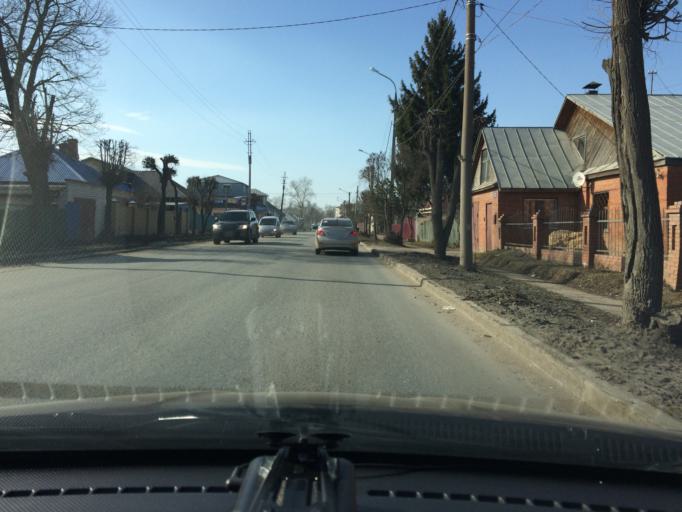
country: RU
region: Mariy-El
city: Yoshkar-Ola
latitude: 56.6468
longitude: 47.9061
